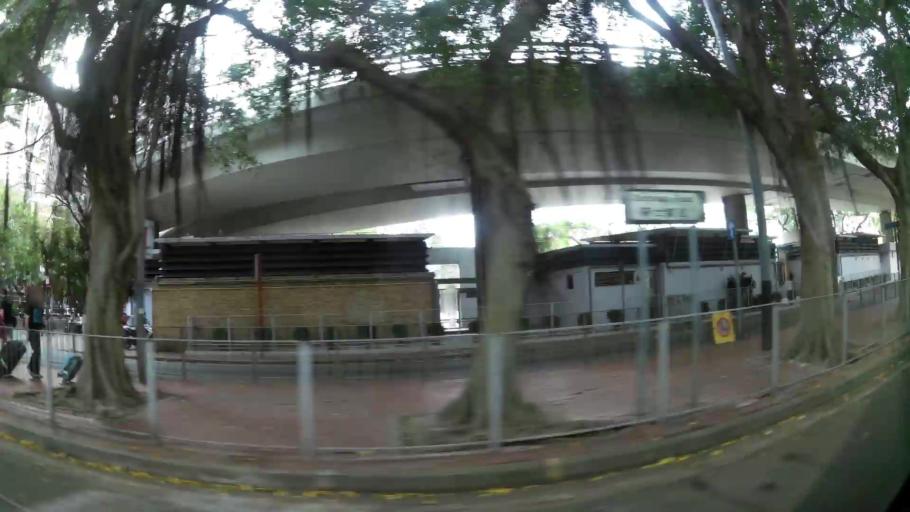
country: HK
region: Wanchai
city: Wan Chai
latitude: 22.2796
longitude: 114.1877
